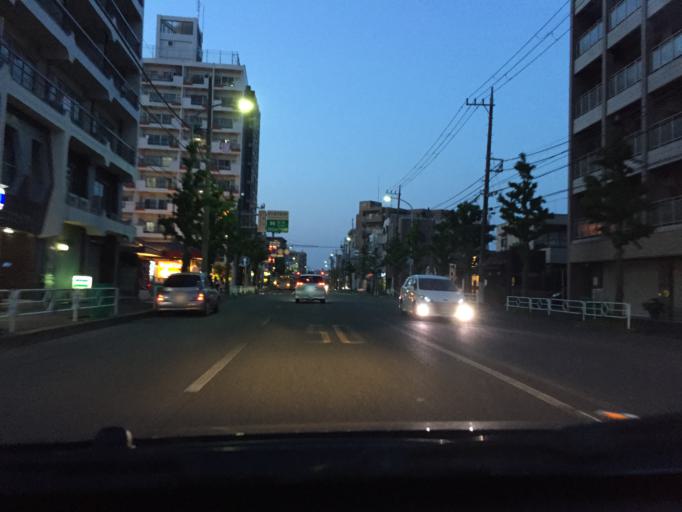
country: JP
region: Kanagawa
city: Yokohama
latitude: 35.4152
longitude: 139.5978
